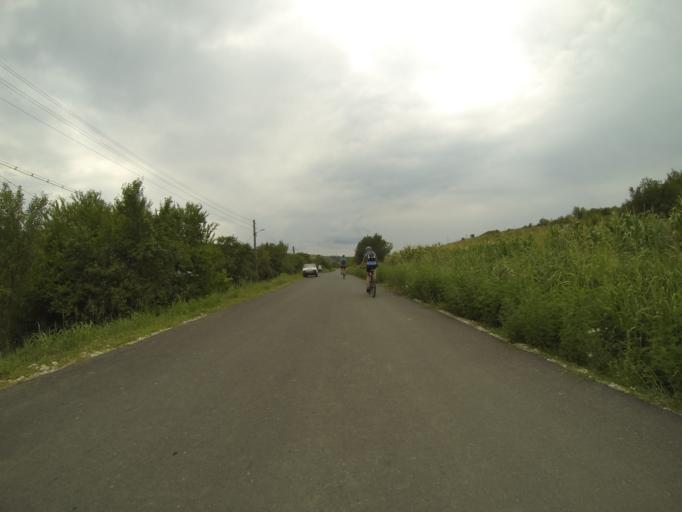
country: RO
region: Dolj
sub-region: Comuna Bradesti
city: Bradesti
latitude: 44.4945
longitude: 23.6658
